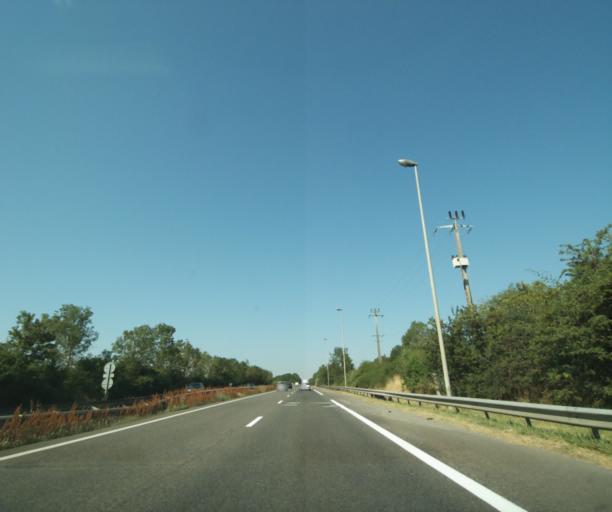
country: FR
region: Lorraine
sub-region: Departement de Meurthe-et-Moselle
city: Gondreville
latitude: 48.6827
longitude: 5.9451
